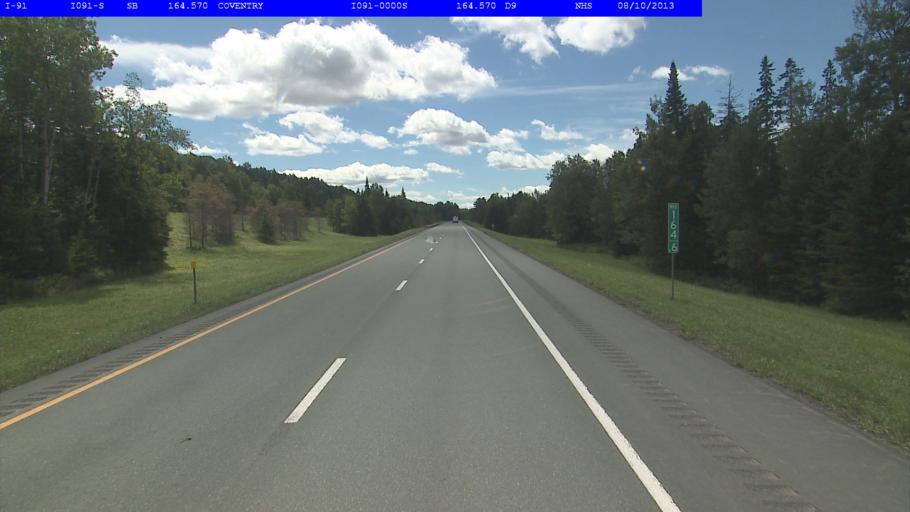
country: US
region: Vermont
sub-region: Orleans County
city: Newport
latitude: 44.8489
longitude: -72.1939
